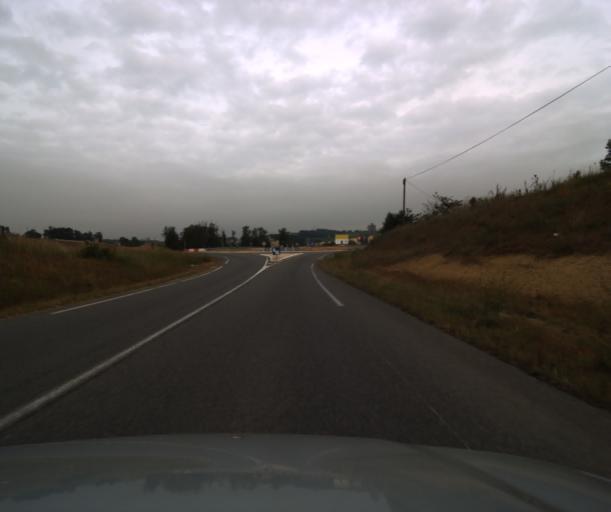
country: FR
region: Midi-Pyrenees
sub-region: Departement du Gers
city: Aubiet
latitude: 43.6478
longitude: 0.7255
